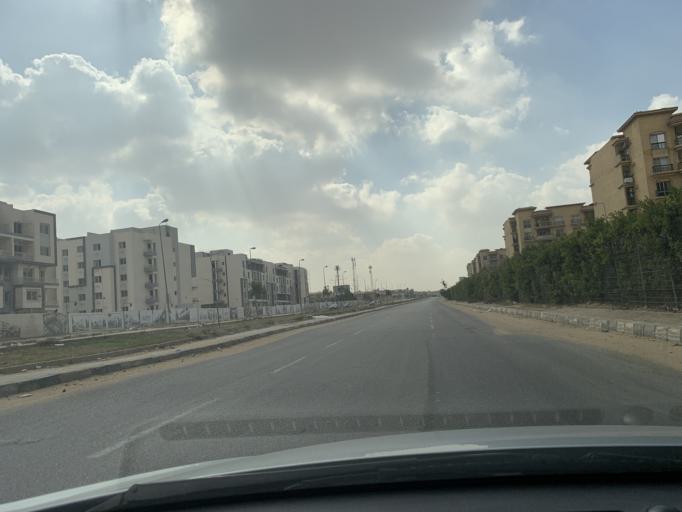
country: EG
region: Muhafazat al Qalyubiyah
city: Al Khankah
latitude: 30.0657
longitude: 31.5192
